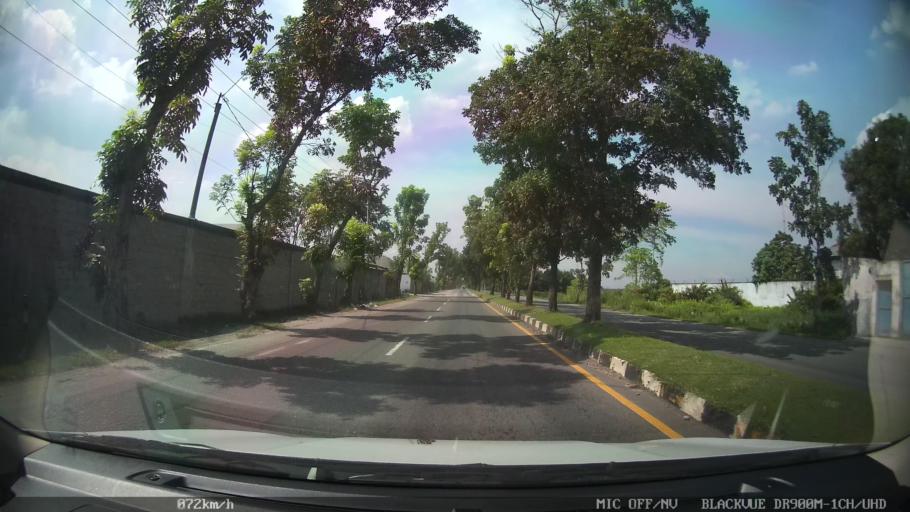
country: ID
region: North Sumatra
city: Binjai
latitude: 3.6194
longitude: 98.5345
